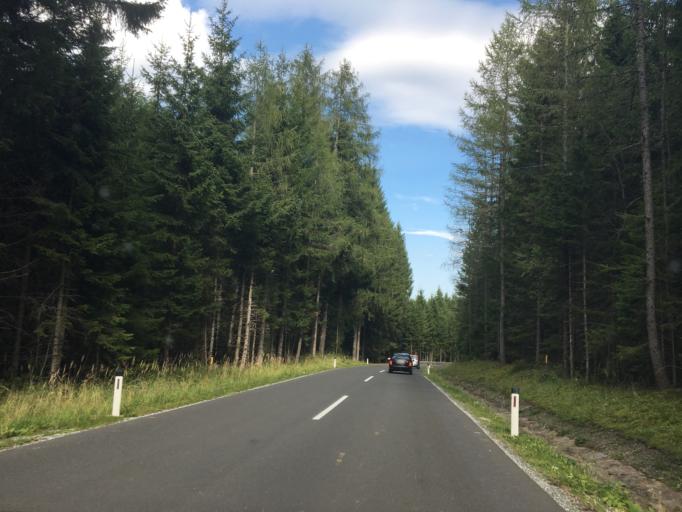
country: AT
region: Styria
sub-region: Politischer Bezirk Deutschlandsberg
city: Gressenberg
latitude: 46.8292
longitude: 15.0957
